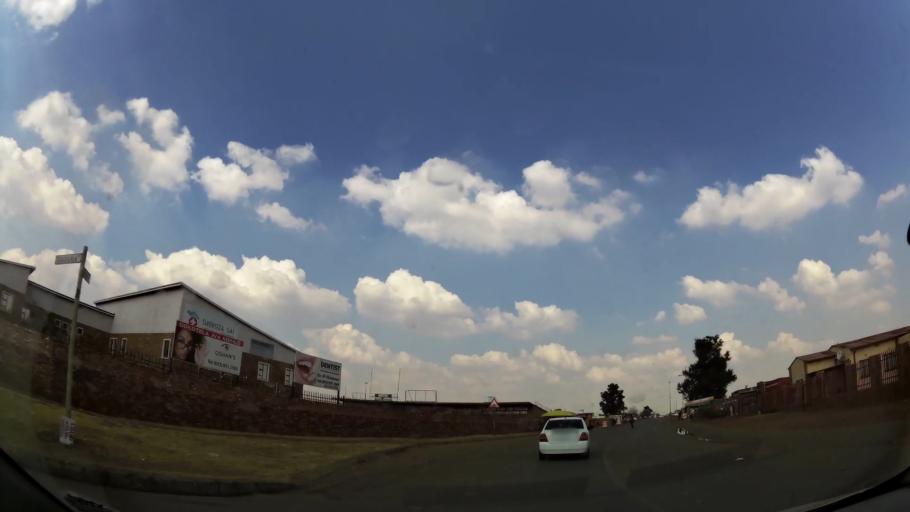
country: ZA
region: Gauteng
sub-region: Ekurhuleni Metropolitan Municipality
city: Germiston
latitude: -26.3475
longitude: 28.1401
